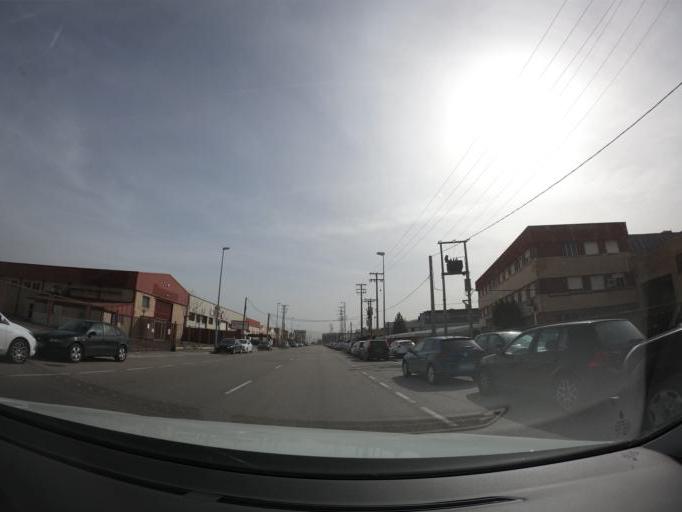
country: ES
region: Basque Country
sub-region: Provincia de Alava
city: Oyon
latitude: 42.4773
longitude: -2.4048
